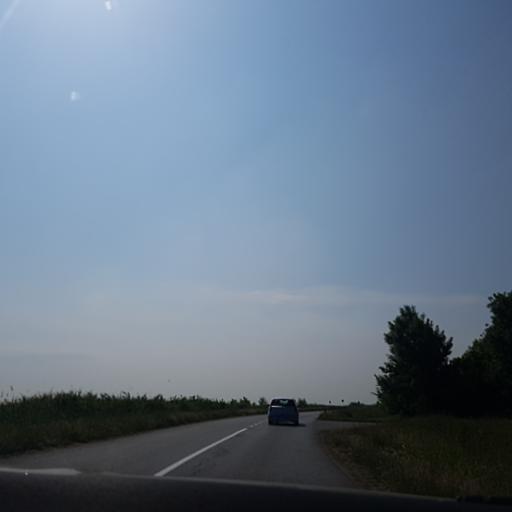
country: RS
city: Neuzina
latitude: 45.3405
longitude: 20.7202
